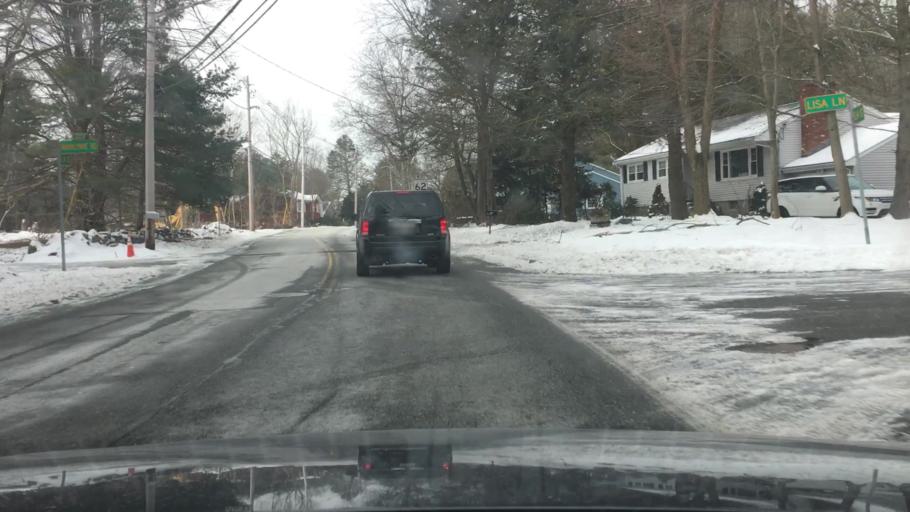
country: US
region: Massachusetts
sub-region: Essex County
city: Middleton
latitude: 42.5756
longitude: -71.0394
